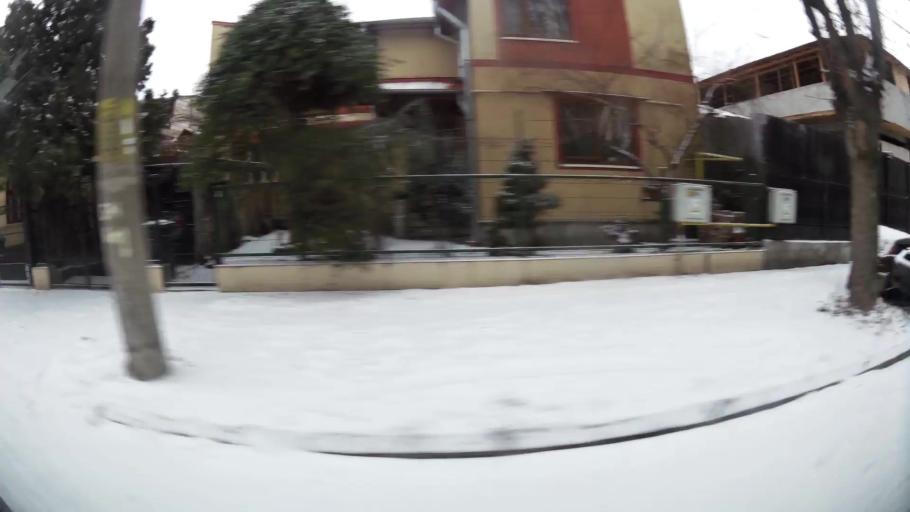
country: RO
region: Prahova
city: Ploiesti
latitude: 44.9363
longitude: 26.0426
